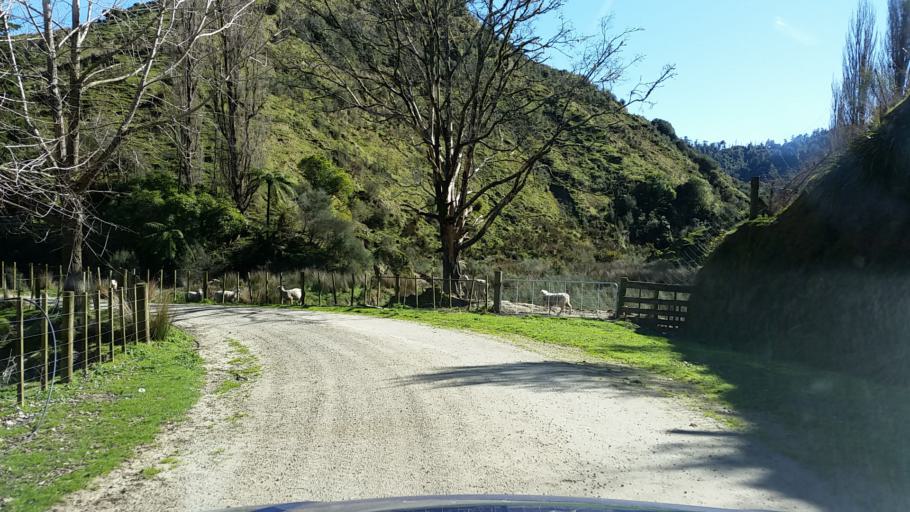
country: NZ
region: Manawatu-Wanganui
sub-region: Wanganui District
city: Wanganui
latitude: -39.6761
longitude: 174.8563
